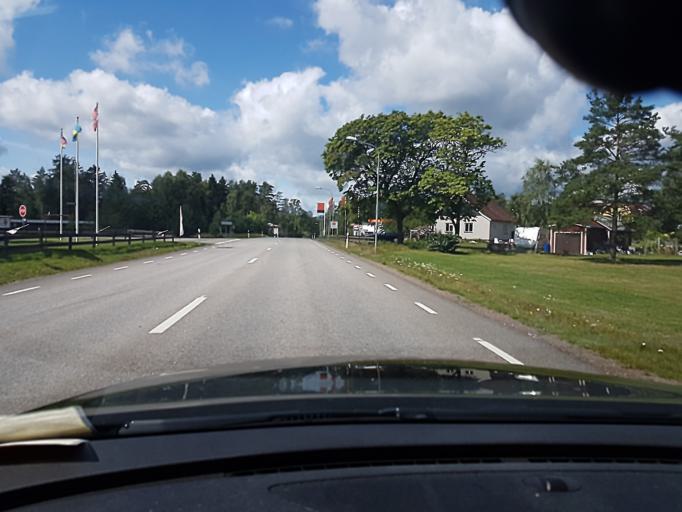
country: SE
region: Kalmar
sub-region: Emmaboda Kommun
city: Emmaboda
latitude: 56.7343
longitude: 15.4829
